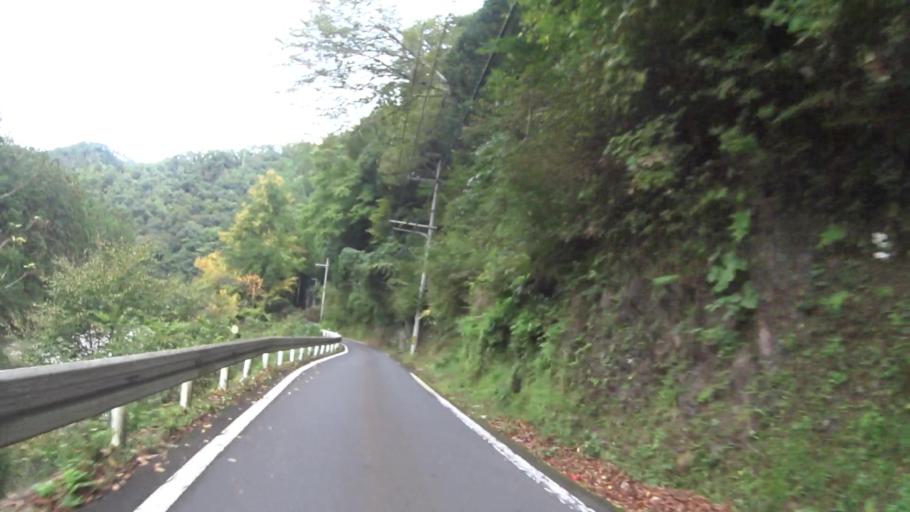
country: JP
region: Fukui
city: Obama
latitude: 35.3194
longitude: 135.6906
